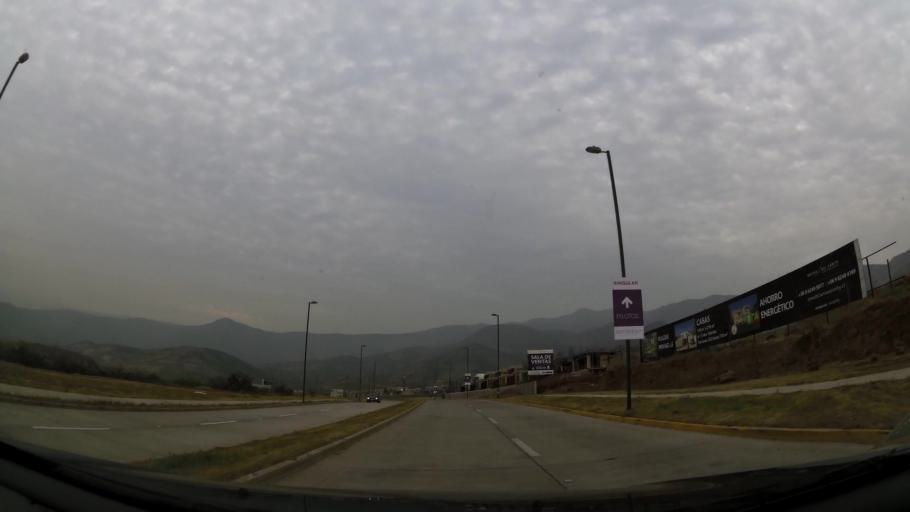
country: CL
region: Santiago Metropolitan
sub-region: Provincia de Chacabuco
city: Chicureo Abajo
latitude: -33.3248
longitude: -70.6372
